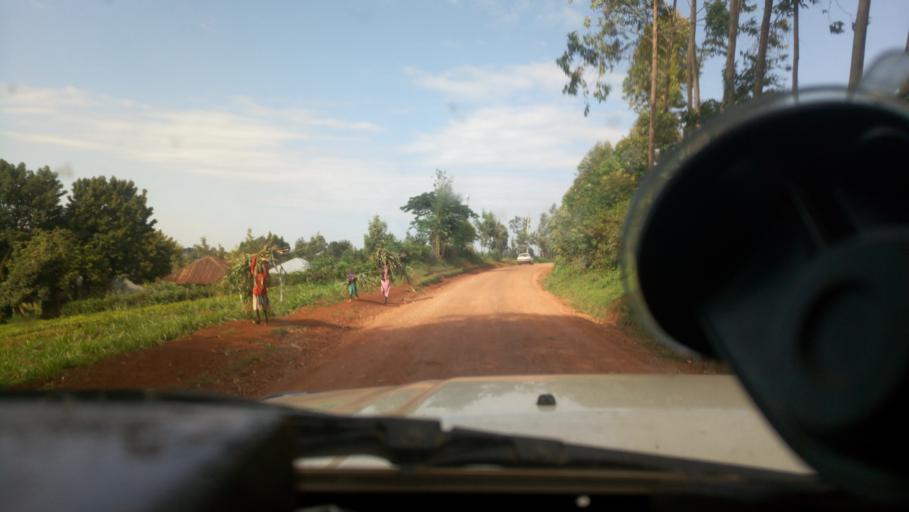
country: KE
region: Nyamira District
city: Nyamira
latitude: -0.6229
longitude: 34.9462
